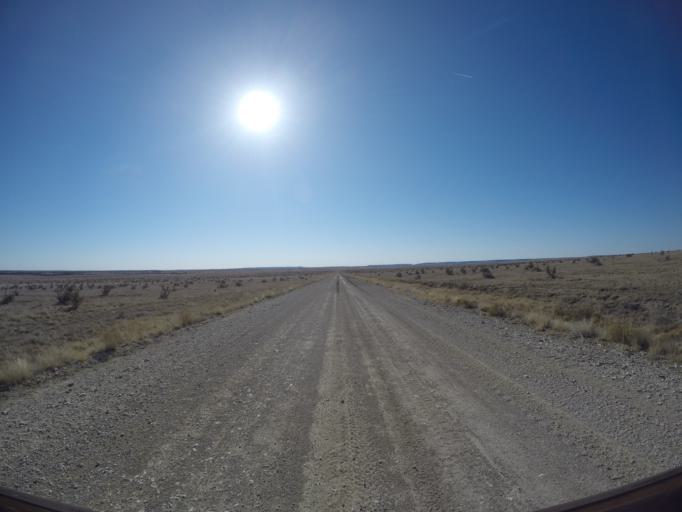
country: US
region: Colorado
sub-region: Otero County
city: La Junta
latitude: 37.7294
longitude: -103.6206
